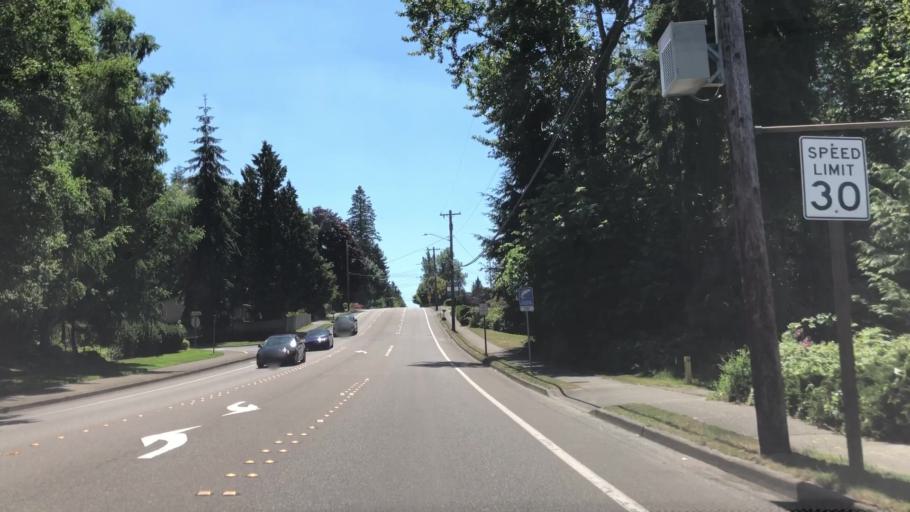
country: US
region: Washington
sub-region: Snohomish County
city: Alderwood Manor
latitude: 47.8456
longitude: -122.2926
